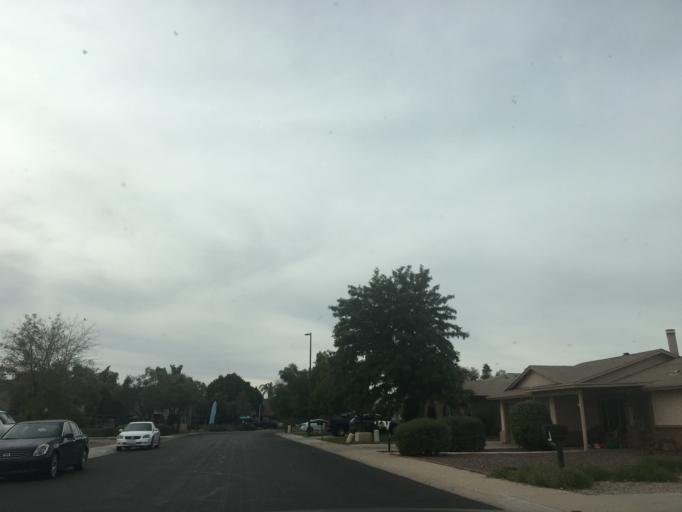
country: US
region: Arizona
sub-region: Maricopa County
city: Gilbert
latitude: 33.3605
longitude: -111.7867
